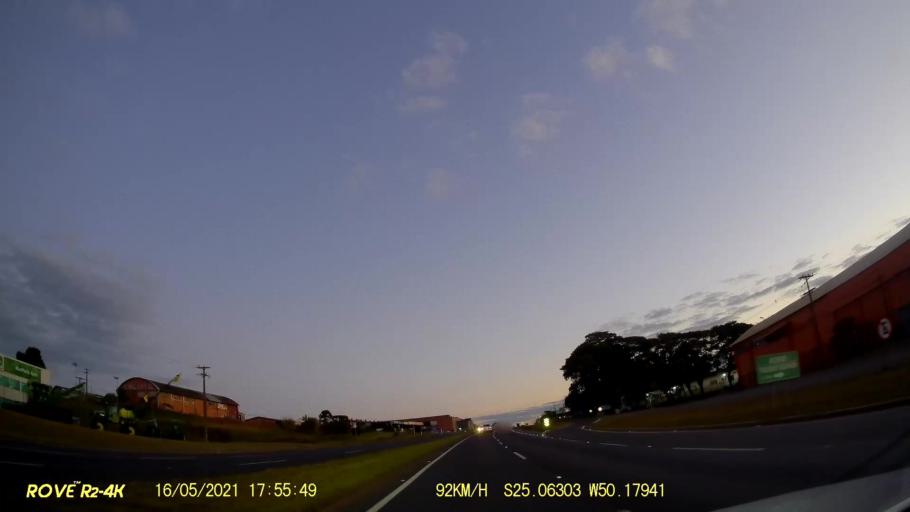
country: BR
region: Parana
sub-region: Ponta Grossa
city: Ponta Grossa
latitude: -25.0630
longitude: -50.1794
